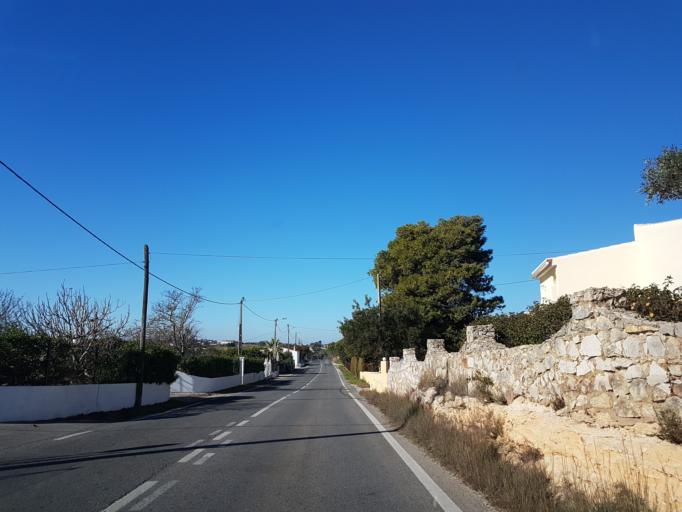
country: PT
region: Faro
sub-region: Lagoa
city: Carvoeiro
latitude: 37.1111
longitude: -8.4466
